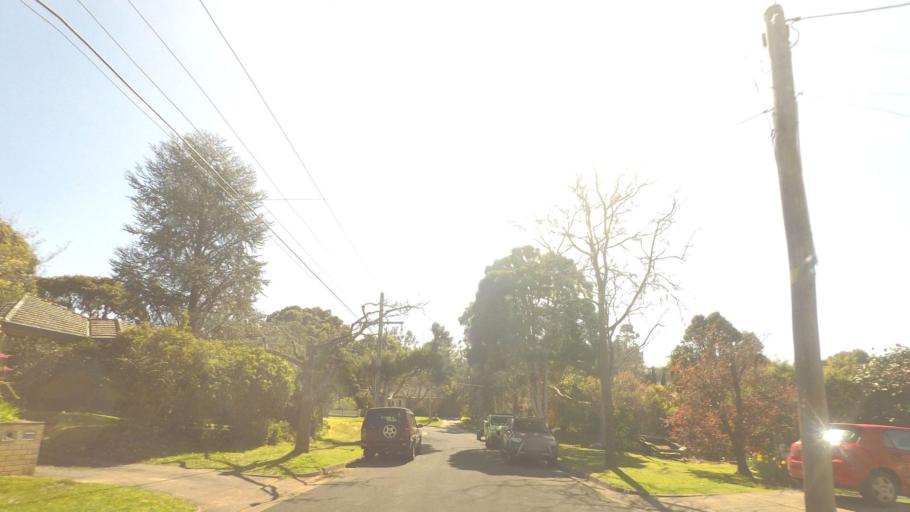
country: AU
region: Victoria
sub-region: Maroondah
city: Heathmont
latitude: -37.8347
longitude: 145.2416
